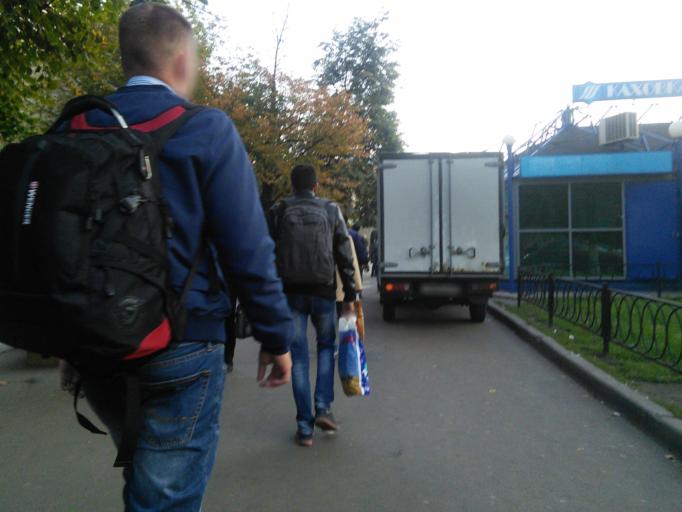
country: RU
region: Moskovskaya
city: Leninskiye Gory
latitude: 55.6883
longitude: 37.5747
